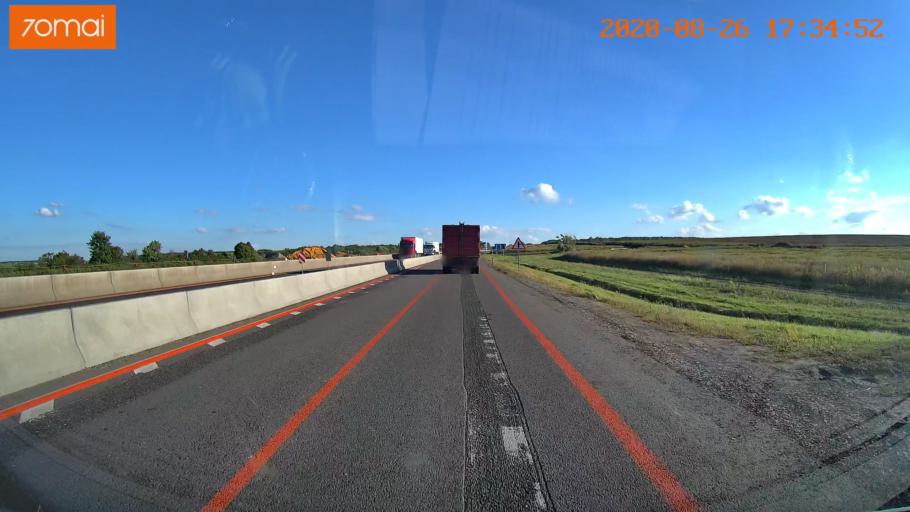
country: RU
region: Tula
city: Kazachka
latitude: 53.3945
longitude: 38.1843
